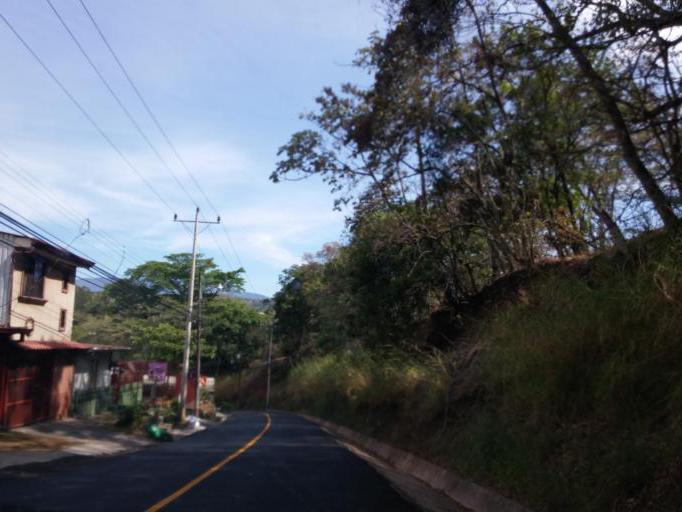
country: CR
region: Alajuela
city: Alajuela
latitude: 10.0316
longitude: -84.2254
